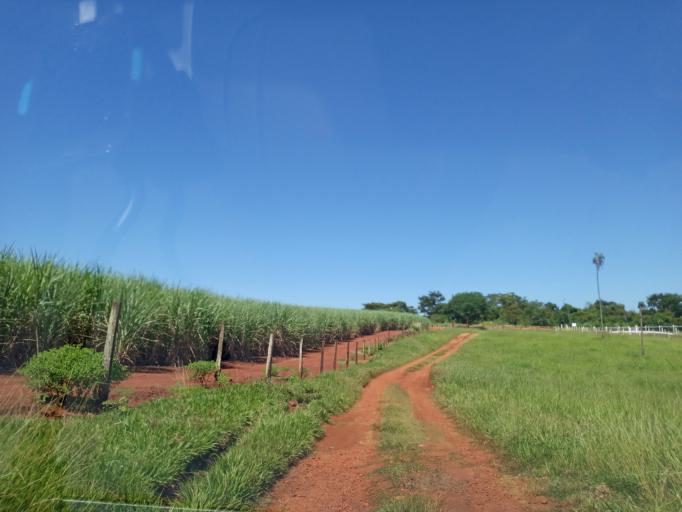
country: BR
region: Goias
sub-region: Itumbiara
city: Itumbiara
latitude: -18.4053
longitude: -49.1415
